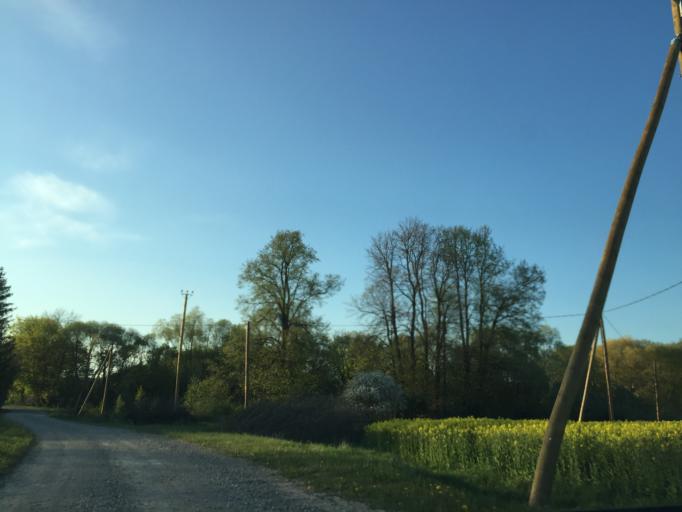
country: LV
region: Bauskas Rajons
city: Bauska
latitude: 56.3167
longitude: 24.1792
